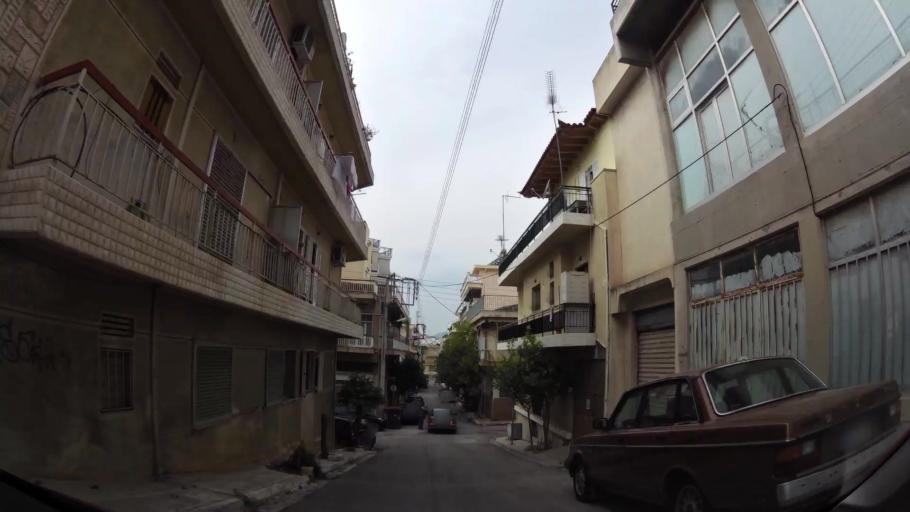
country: GR
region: Attica
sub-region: Nomarchia Athinas
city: Peristeri
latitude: 38.0039
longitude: 23.6834
